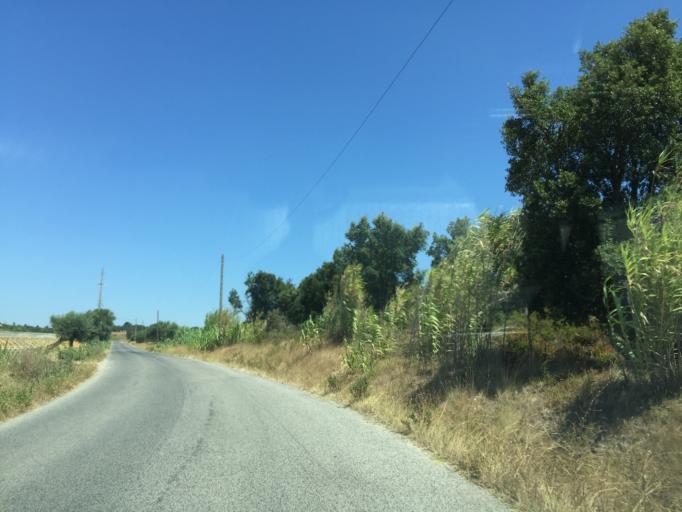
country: PT
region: Lisbon
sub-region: Azambuja
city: Aveiras de Cima
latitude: 39.1461
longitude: -8.8940
